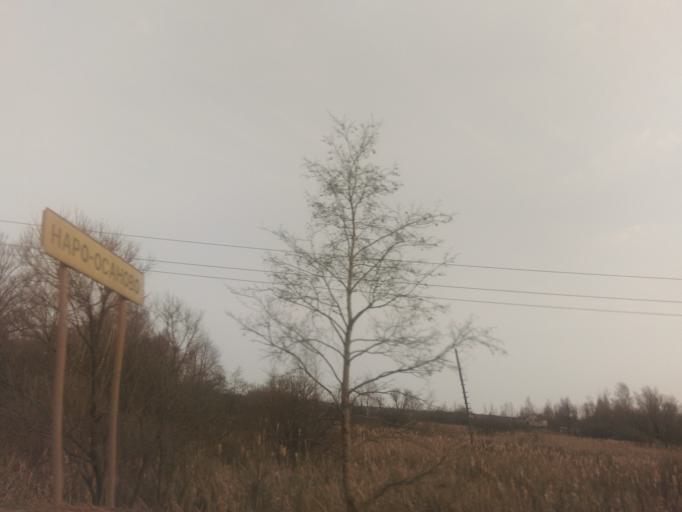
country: RU
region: Moskovskaya
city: Chupryakovo
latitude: 55.5596
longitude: 36.5577
